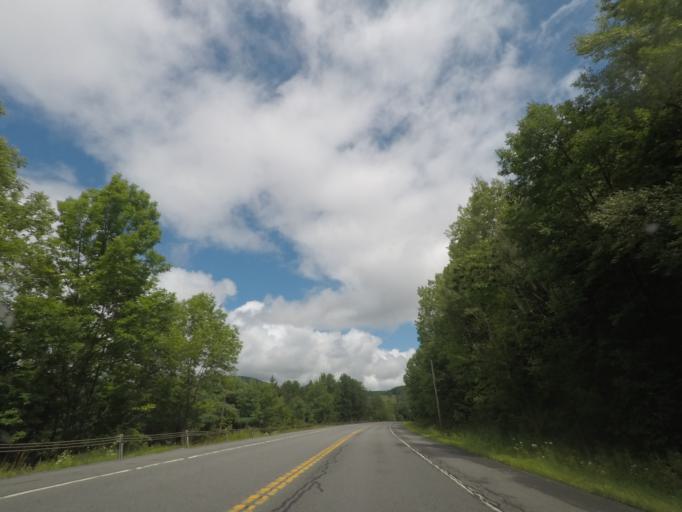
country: US
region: Massachusetts
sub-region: Berkshire County
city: Lanesborough
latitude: 42.6204
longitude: -73.3724
